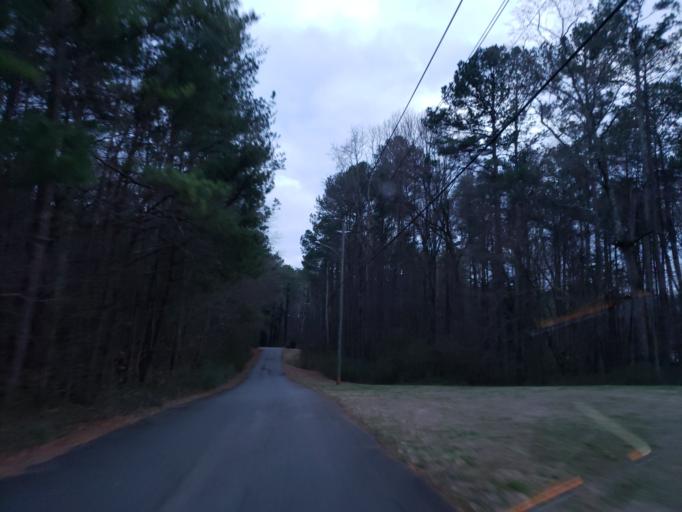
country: US
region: Georgia
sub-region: Cobb County
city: Kennesaw
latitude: 34.0293
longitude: -84.6329
